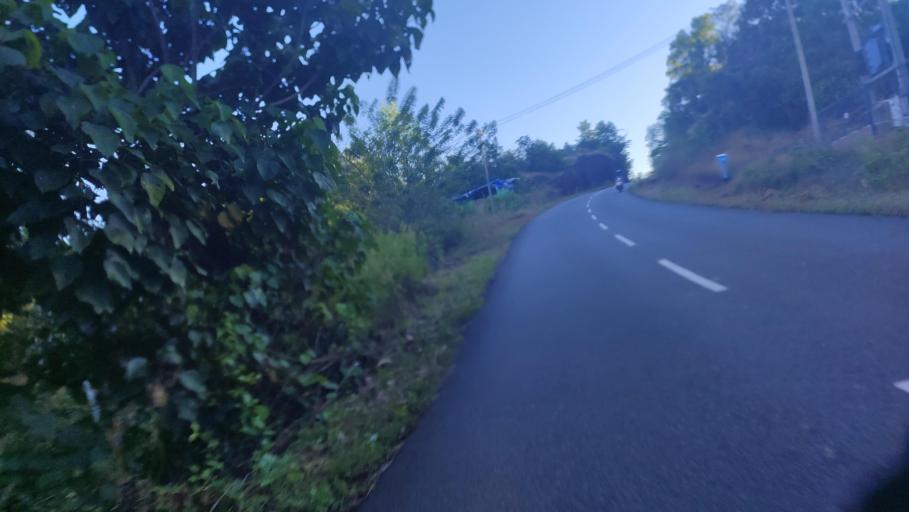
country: IN
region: Kerala
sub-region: Kasaragod District
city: Kasaragod
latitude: 12.4488
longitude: 75.0995
